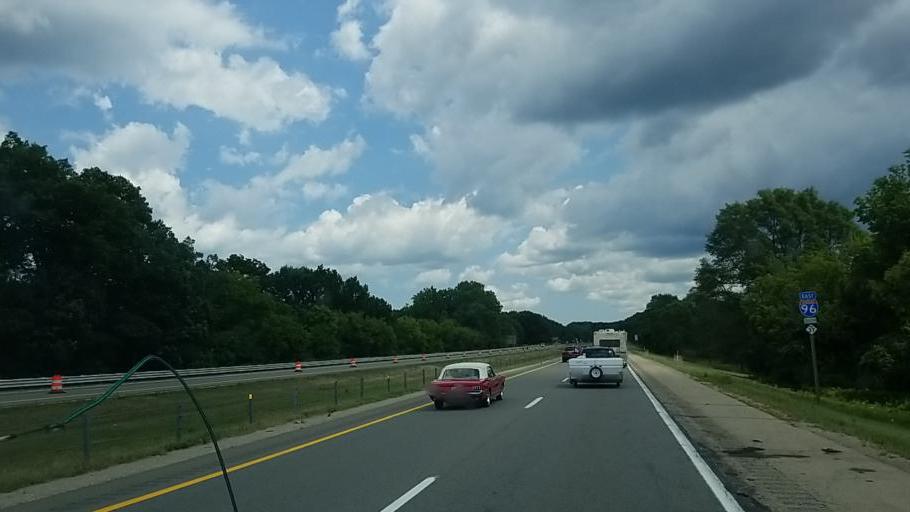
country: US
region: Michigan
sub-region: Kent County
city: Northview
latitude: 43.0168
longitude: -85.6287
